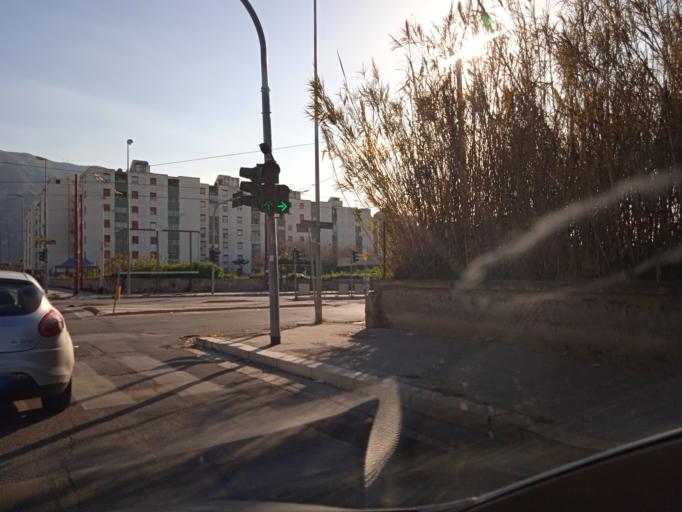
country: IT
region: Sicily
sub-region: Palermo
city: Ciaculli
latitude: 38.0948
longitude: 13.4114
